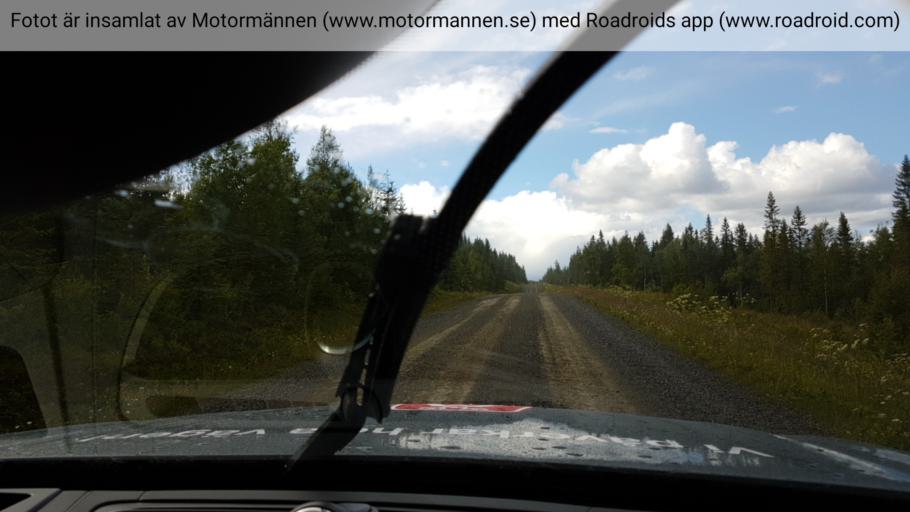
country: SE
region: Jaemtland
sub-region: Bergs Kommun
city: Hoverberg
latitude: 63.0064
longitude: 14.1264
